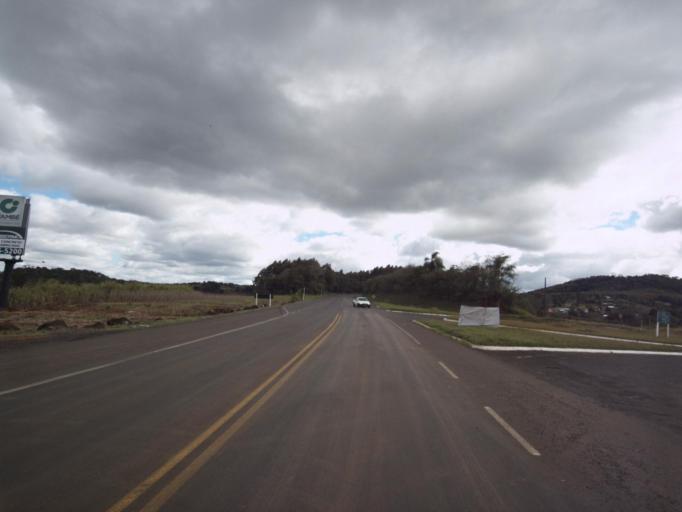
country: BR
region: Santa Catarina
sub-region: Concordia
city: Concordia
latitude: -27.3277
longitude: -51.9791
